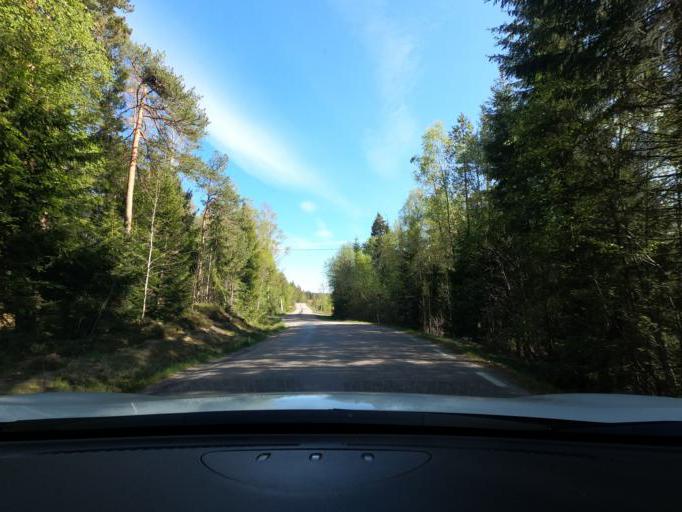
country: SE
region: Vaestra Goetaland
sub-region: Harryda Kommun
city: Hindas
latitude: 57.6622
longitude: 12.3536
